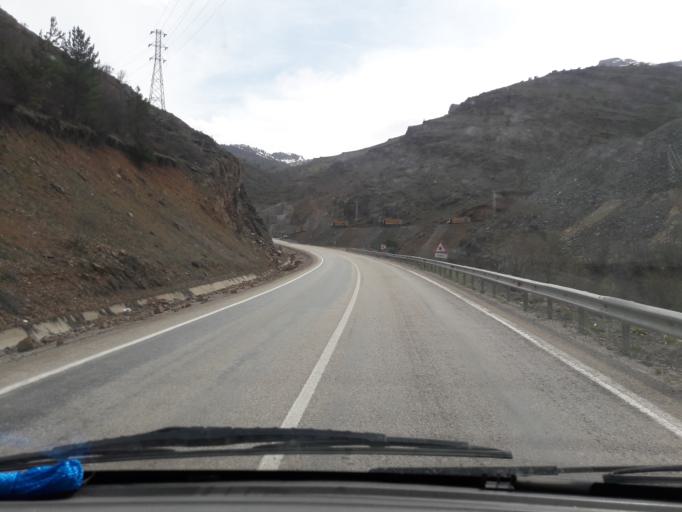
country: TR
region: Gumushane
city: Gumushkhane
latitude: 40.3033
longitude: 39.4754
